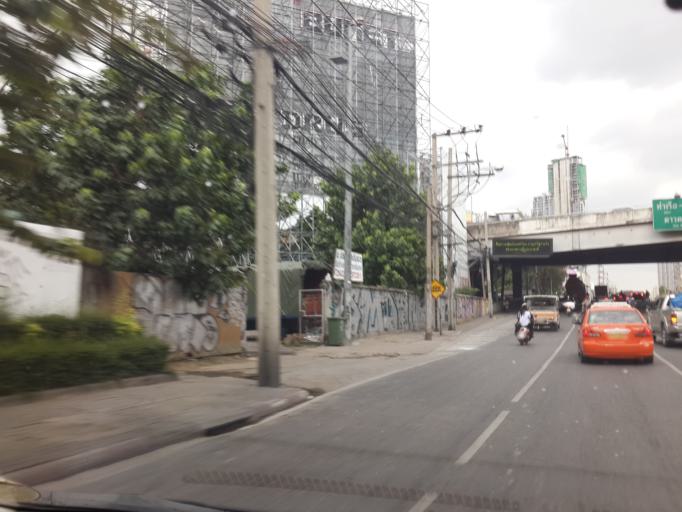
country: TH
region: Bangkok
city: Ratchathewi
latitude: 13.7497
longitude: 100.5491
